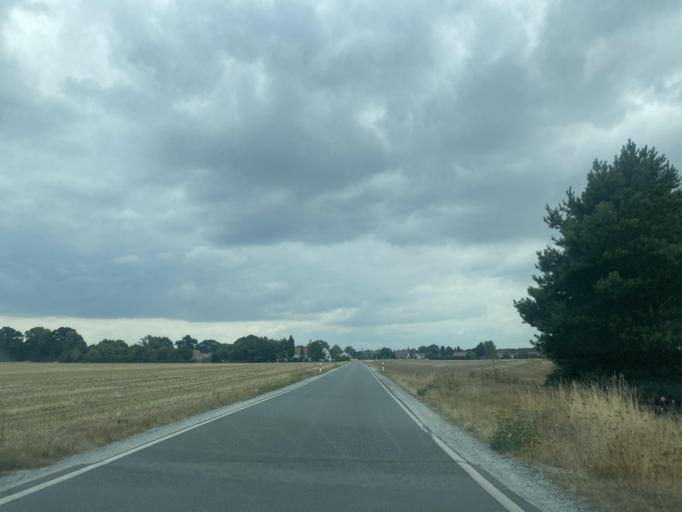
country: DE
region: Saxony
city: Konigswartha
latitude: 51.2960
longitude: 14.3182
